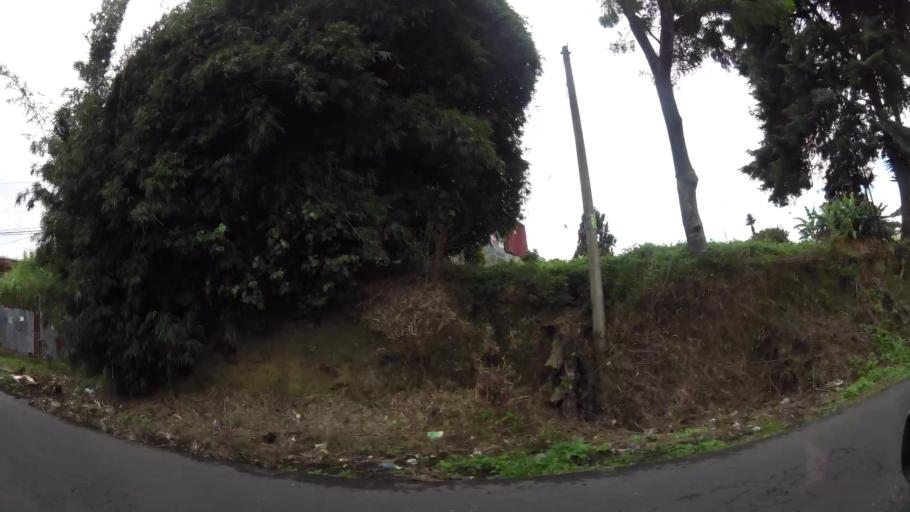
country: CR
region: San Jose
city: Ipis
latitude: 9.9585
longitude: -84.0193
